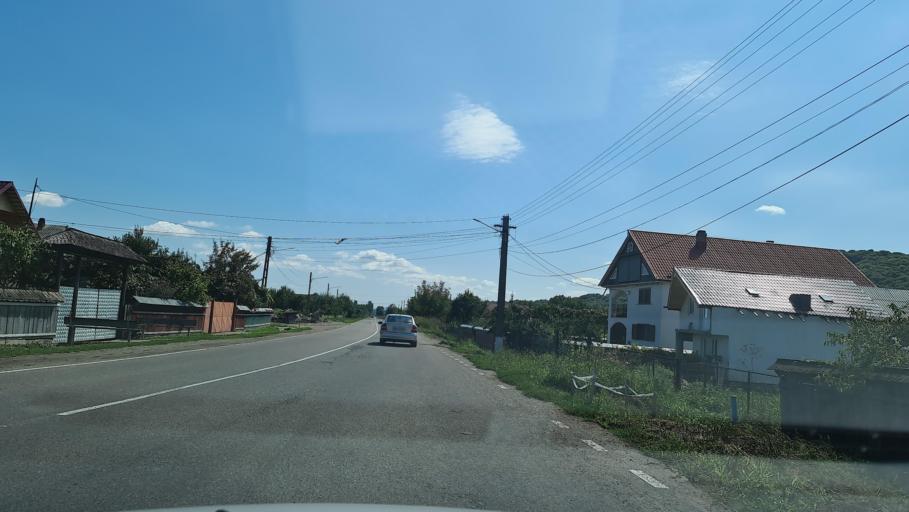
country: RO
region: Neamt
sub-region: Comuna Tazlau
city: Tazlau
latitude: 46.7099
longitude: 26.4855
